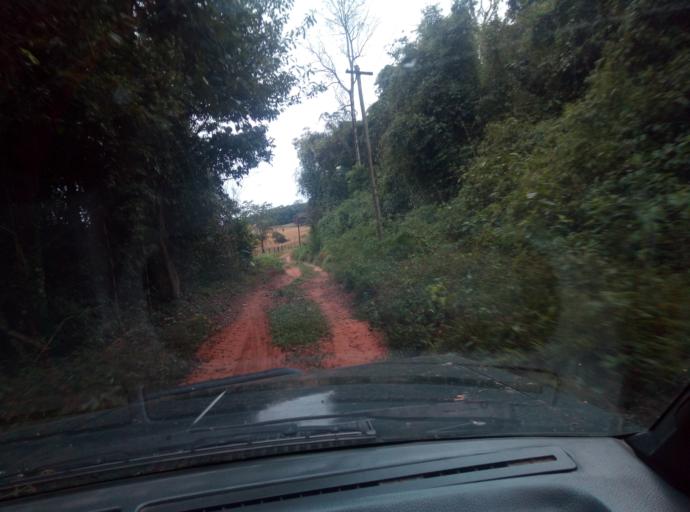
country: PY
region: Caaguazu
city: Carayao
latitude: -25.1893
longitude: -56.3445
